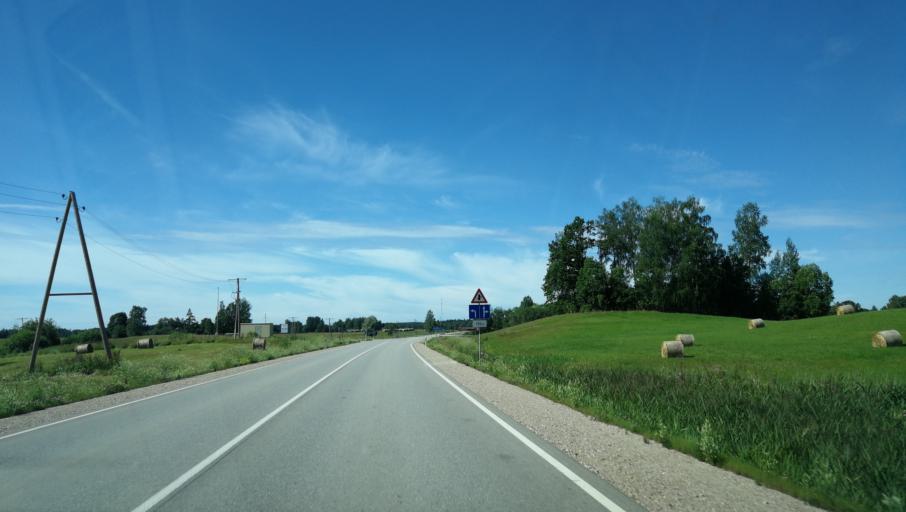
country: LV
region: Gulbenes Rajons
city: Gulbene
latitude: 57.0849
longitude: 26.6136
